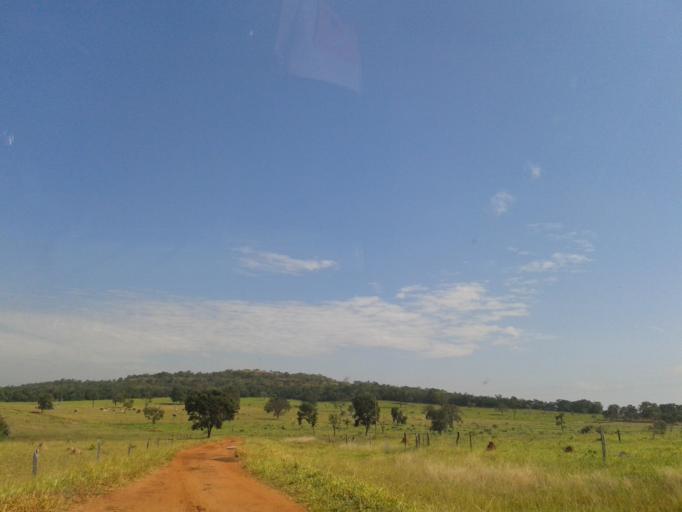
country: BR
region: Minas Gerais
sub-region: Campina Verde
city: Campina Verde
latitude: -19.3909
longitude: -49.6304
